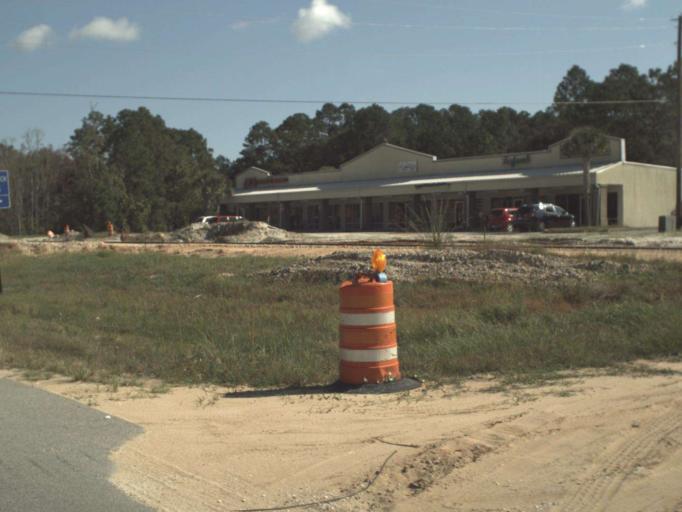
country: US
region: Florida
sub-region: Walton County
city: Freeport
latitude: 30.4822
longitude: -86.1248
